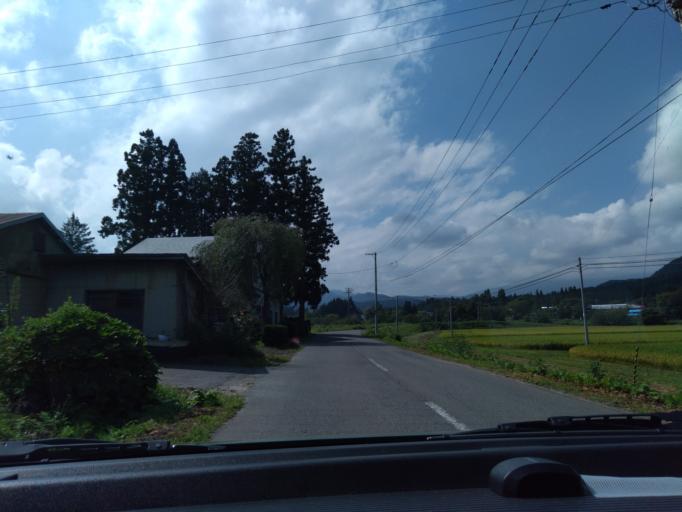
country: JP
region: Iwate
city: Shizukuishi
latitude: 39.6832
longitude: 140.9146
